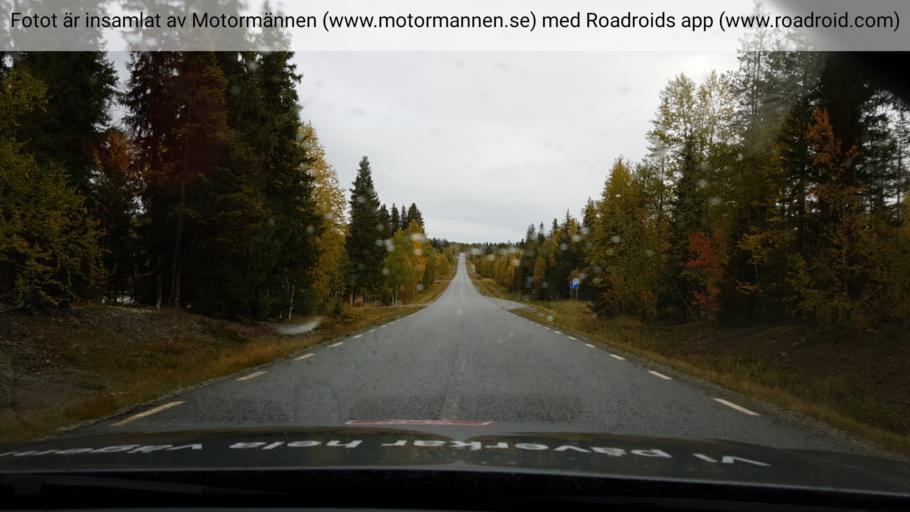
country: SE
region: Vaesterbotten
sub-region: Vilhelmina Kommun
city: Sjoberg
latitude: 64.7962
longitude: 16.0521
